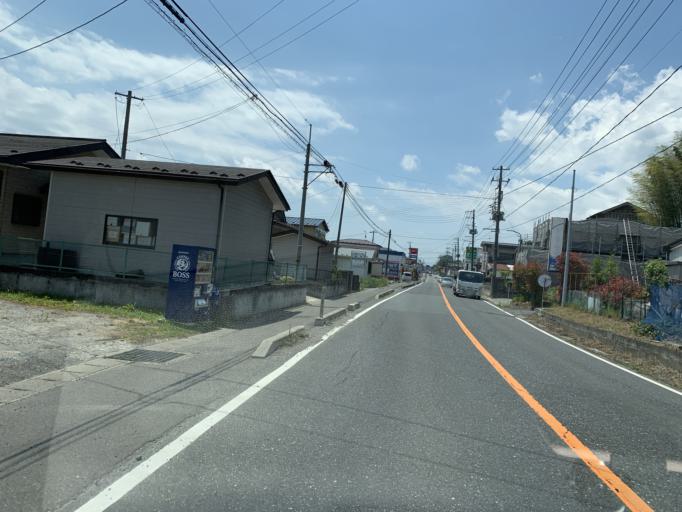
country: JP
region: Miyagi
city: Wakuya
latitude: 38.4826
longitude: 141.0981
